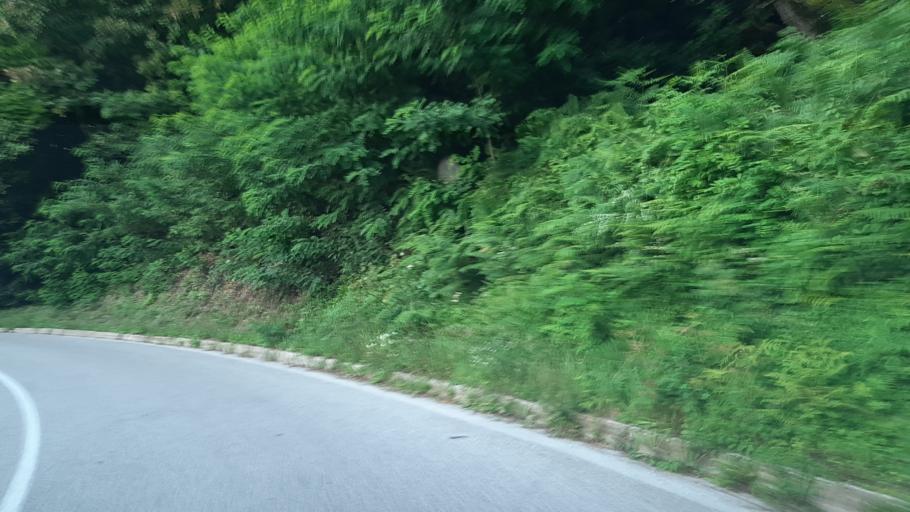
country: SI
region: Dobje
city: Dobje pri Planini
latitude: 46.1431
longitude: 15.4475
